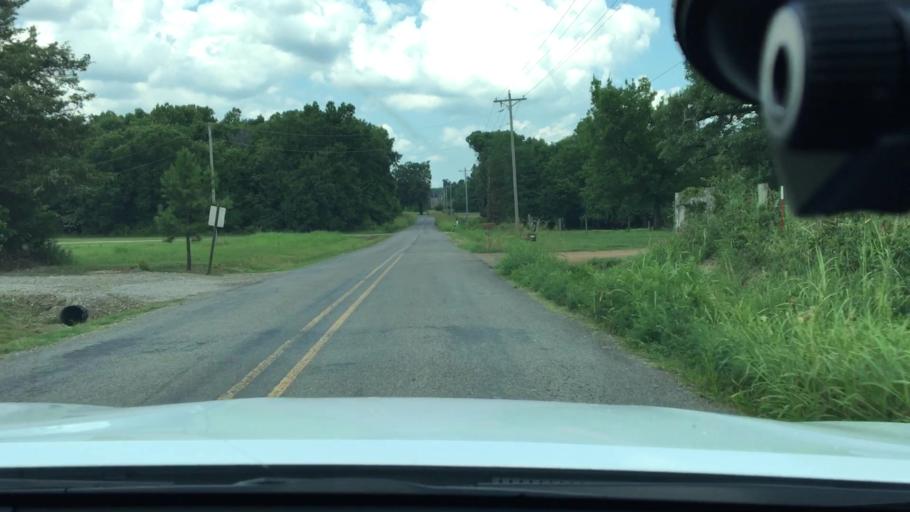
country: US
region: Arkansas
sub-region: Logan County
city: Paris
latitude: 35.2690
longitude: -93.6604
